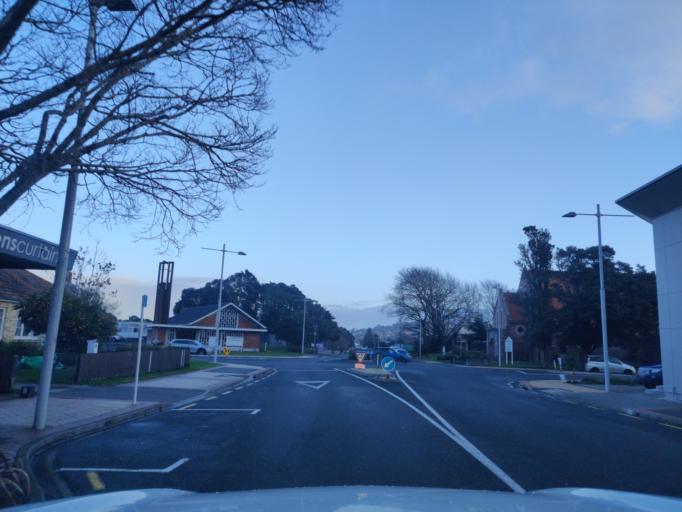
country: NZ
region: Auckland
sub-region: Auckland
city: Pukekohe East
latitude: -37.2014
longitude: 174.9011
